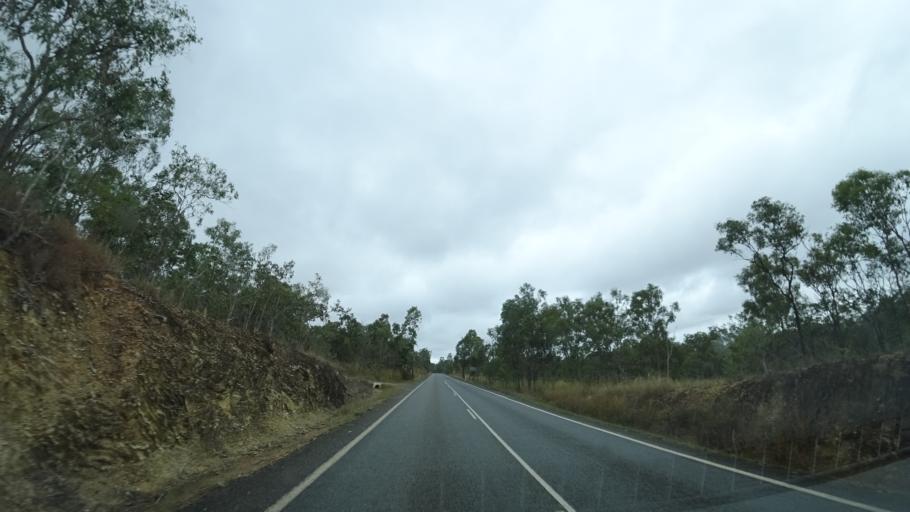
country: AU
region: Queensland
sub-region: Cairns
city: Port Douglas
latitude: -16.6861
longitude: 145.3329
